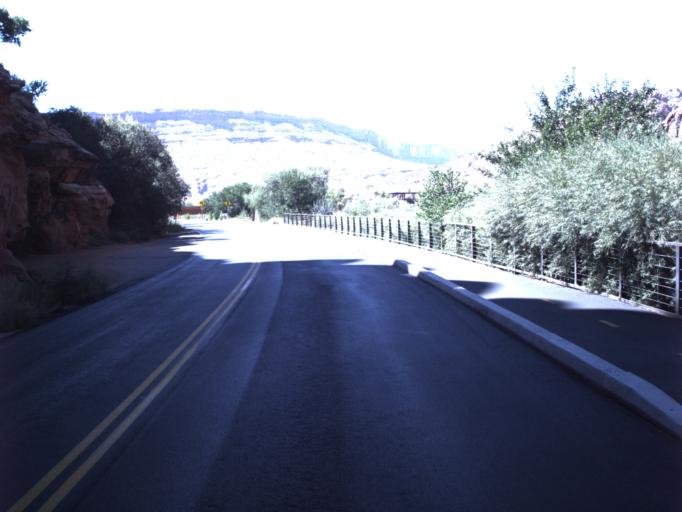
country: US
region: Utah
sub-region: Grand County
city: Moab
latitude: 38.6031
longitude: -109.5719
